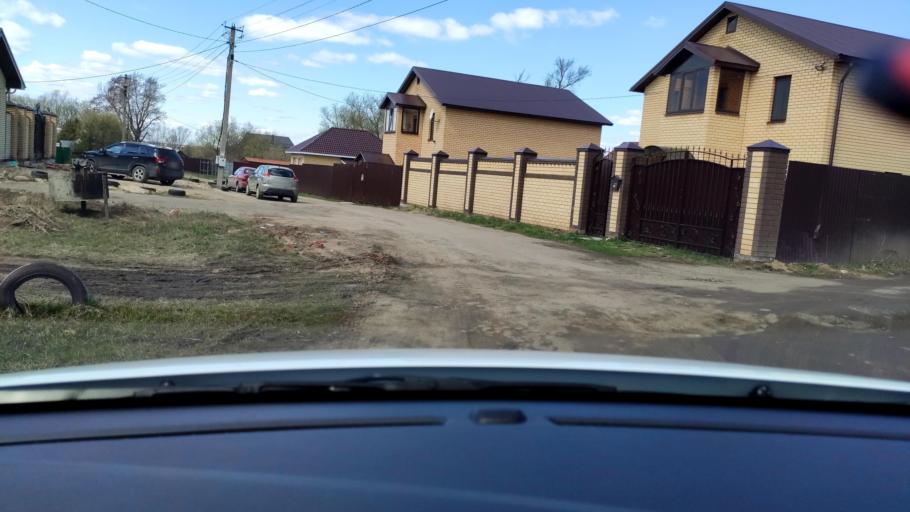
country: RU
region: Tatarstan
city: Stolbishchi
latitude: 55.7180
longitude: 49.3508
